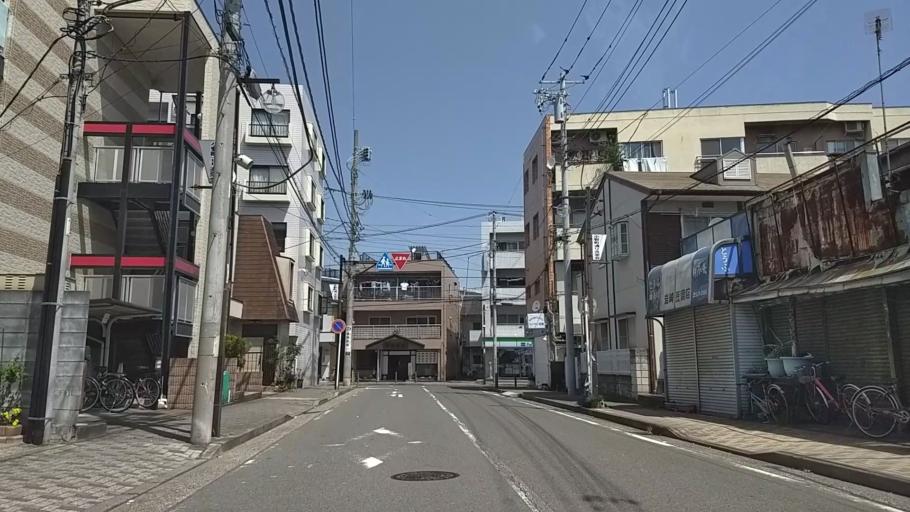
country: JP
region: Kanagawa
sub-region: Kawasaki-shi
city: Kawasaki
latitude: 35.4968
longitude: 139.6834
